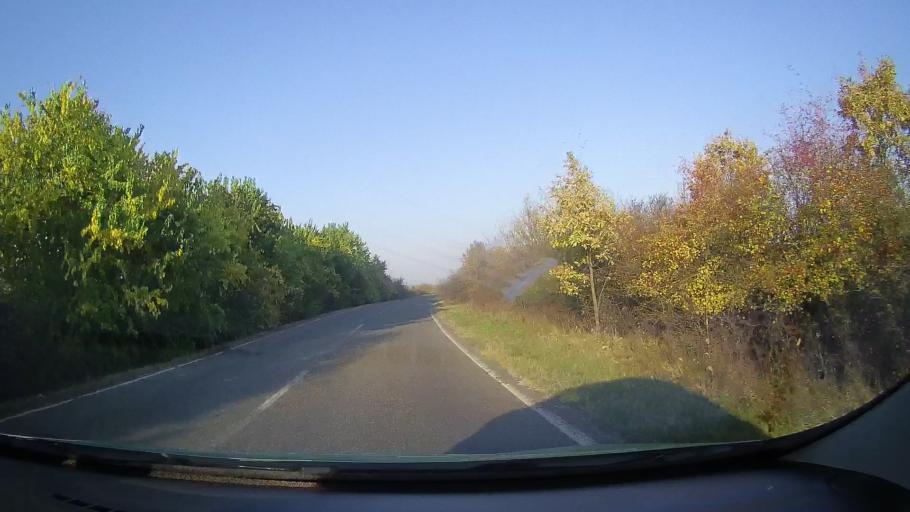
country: RO
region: Arad
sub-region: Comuna Tarnova
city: Chier
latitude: 46.3239
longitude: 21.8307
